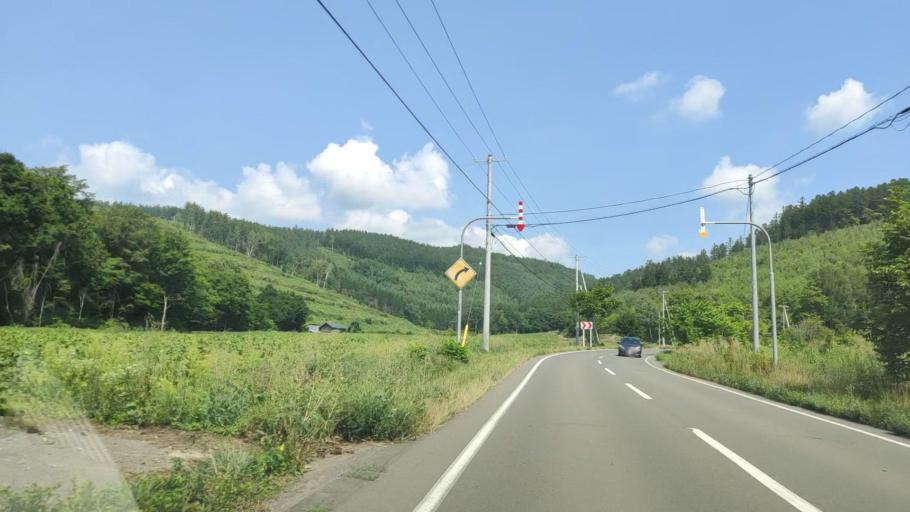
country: JP
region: Hokkaido
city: Shimo-furano
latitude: 43.4243
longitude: 142.4001
